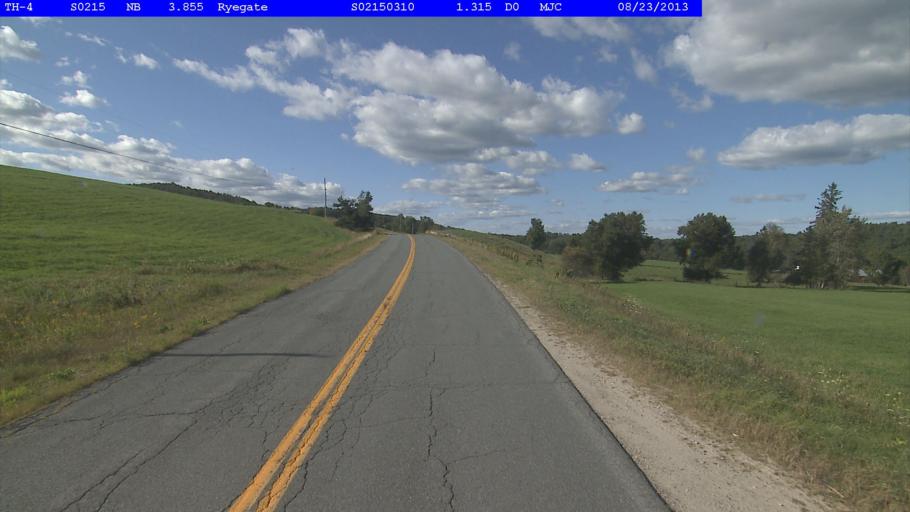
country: US
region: New Hampshire
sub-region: Grafton County
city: Woodsville
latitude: 44.2600
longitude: -72.1707
